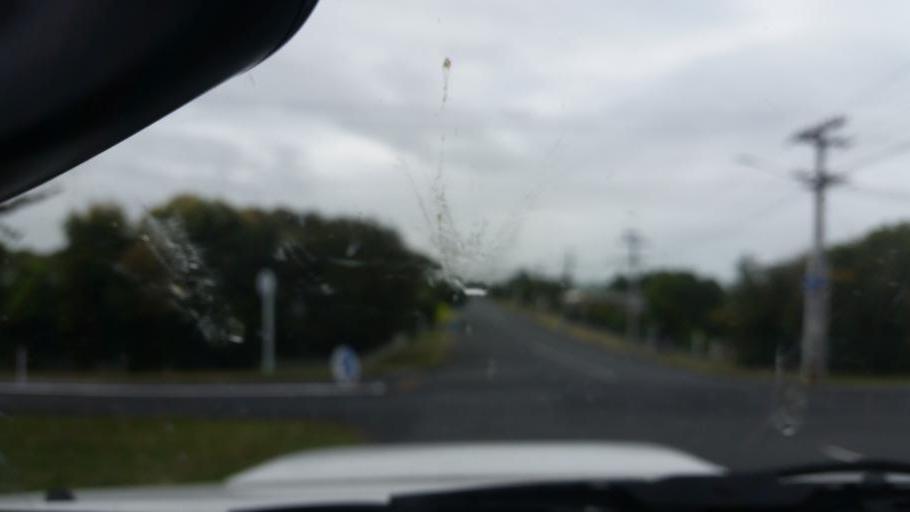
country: NZ
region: Northland
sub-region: Kaipara District
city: Dargaville
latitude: -35.9325
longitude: 173.8719
